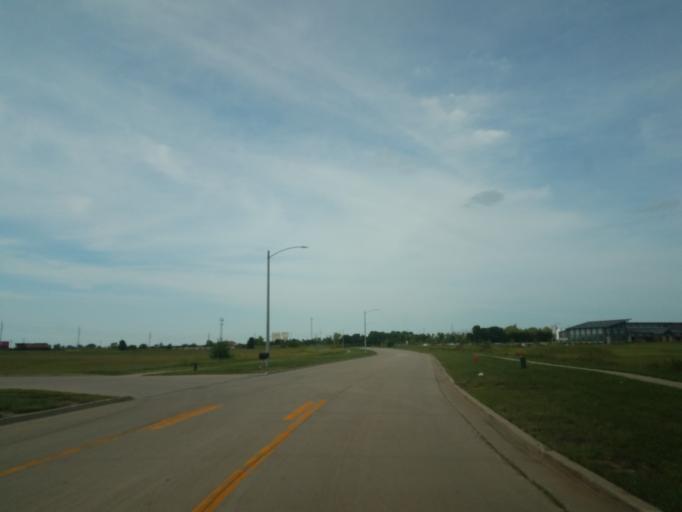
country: US
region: Illinois
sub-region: McLean County
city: Normal
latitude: 40.5268
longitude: -88.9495
